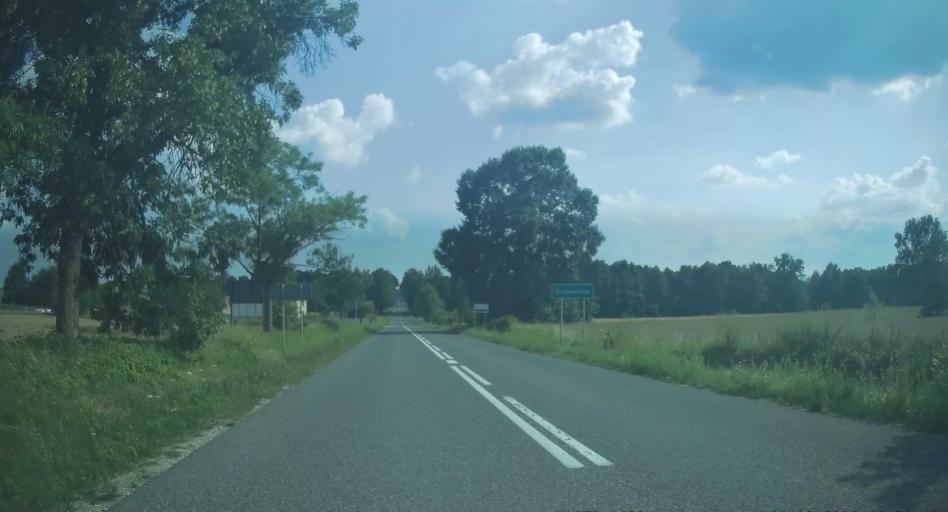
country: PL
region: Swietokrzyskie
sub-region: Powiat kielecki
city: Lopuszno
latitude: 50.9248
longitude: 20.2400
